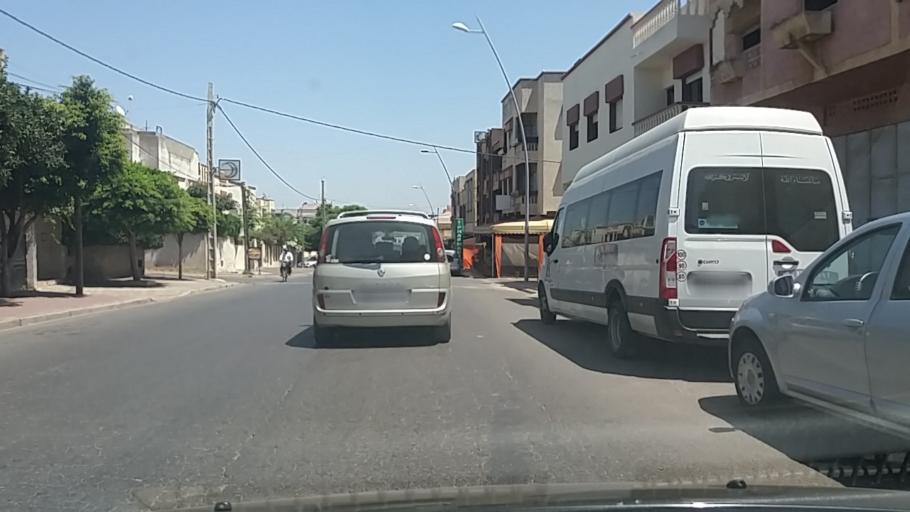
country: MA
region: Gharb-Chrarda-Beni Hssen
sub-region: Kenitra Province
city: Kenitra
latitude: 34.2626
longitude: -6.6181
